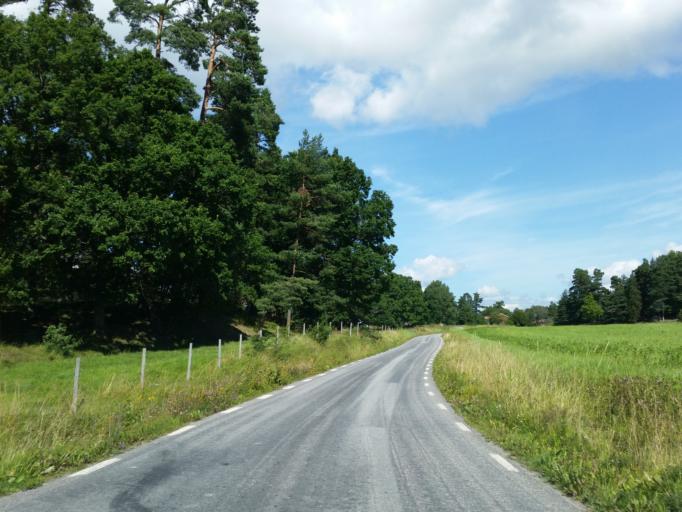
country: SE
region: Soedermanland
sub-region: Trosa Kommun
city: Trosa
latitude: 58.9747
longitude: 17.6523
